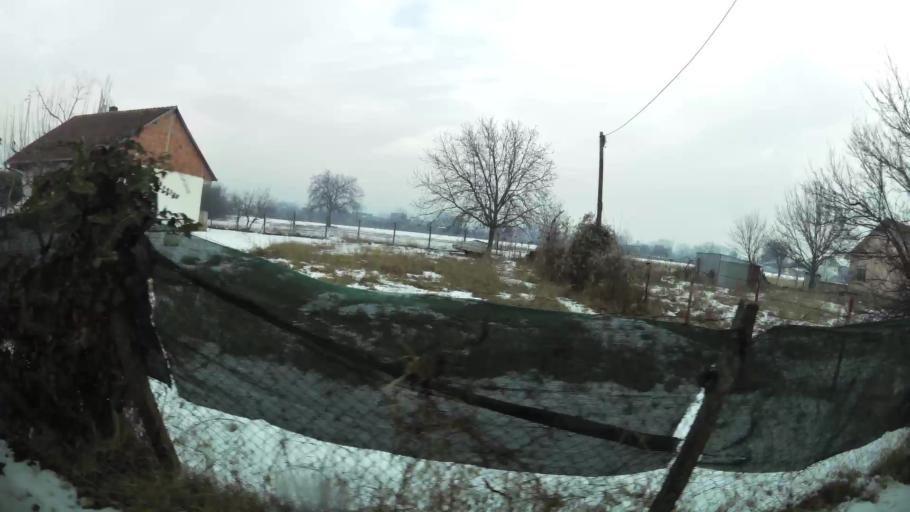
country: MK
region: Saraj
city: Saraj
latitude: 42.0365
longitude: 21.3548
